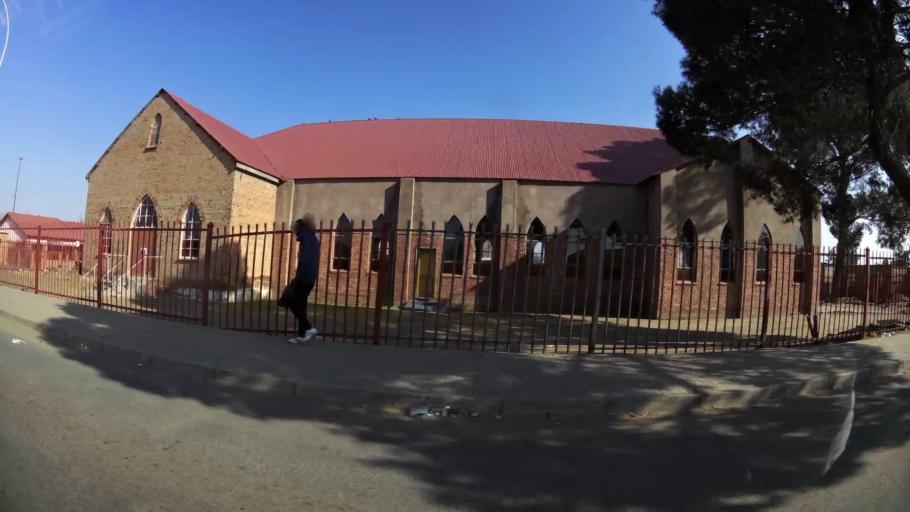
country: ZA
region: Orange Free State
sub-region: Mangaung Metropolitan Municipality
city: Bloemfontein
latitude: -29.1385
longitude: 26.2377
